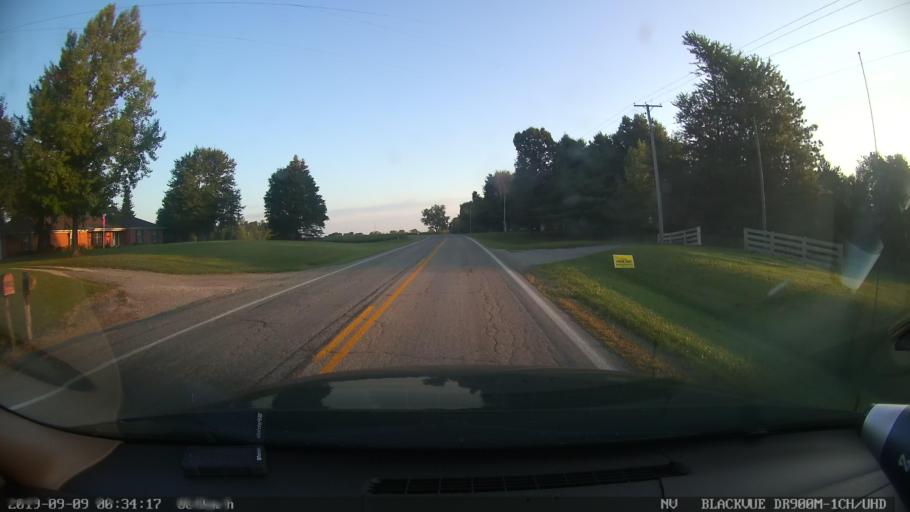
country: US
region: Ohio
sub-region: Crawford County
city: Galion
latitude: 40.6872
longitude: -82.8608
